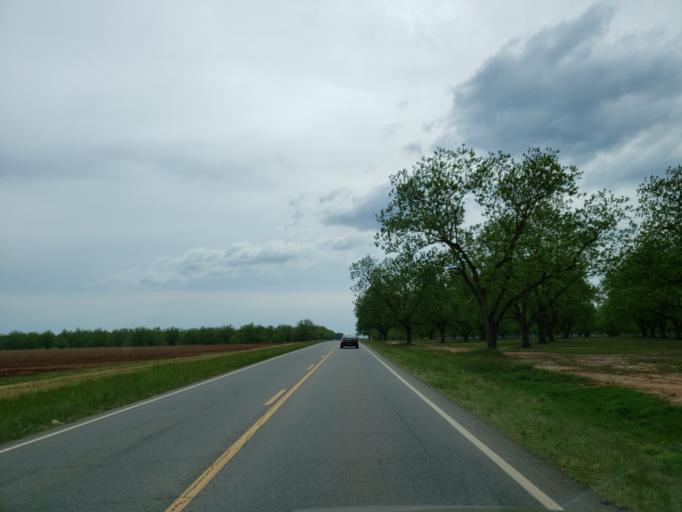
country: US
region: Georgia
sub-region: Houston County
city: Perry
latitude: 32.4366
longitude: -83.7984
